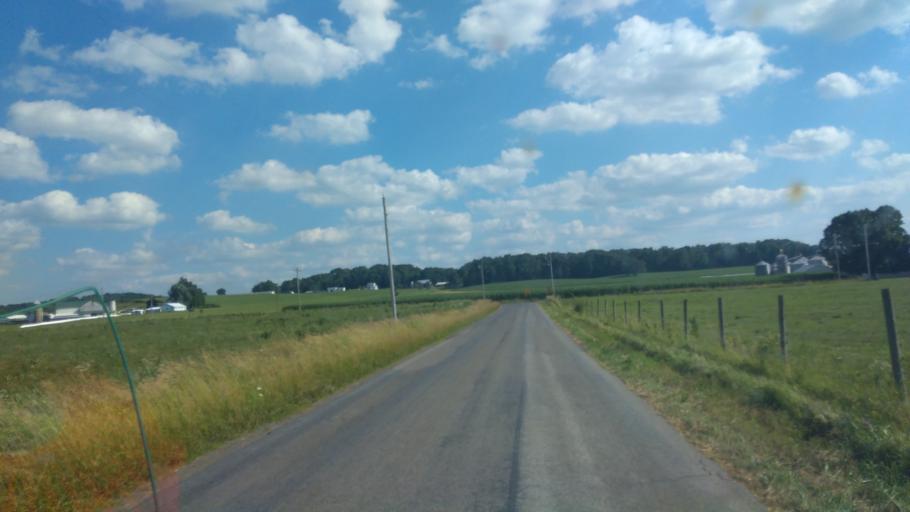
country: US
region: Ohio
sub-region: Wayne County
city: Apple Creek
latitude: 40.7277
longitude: -81.8438
